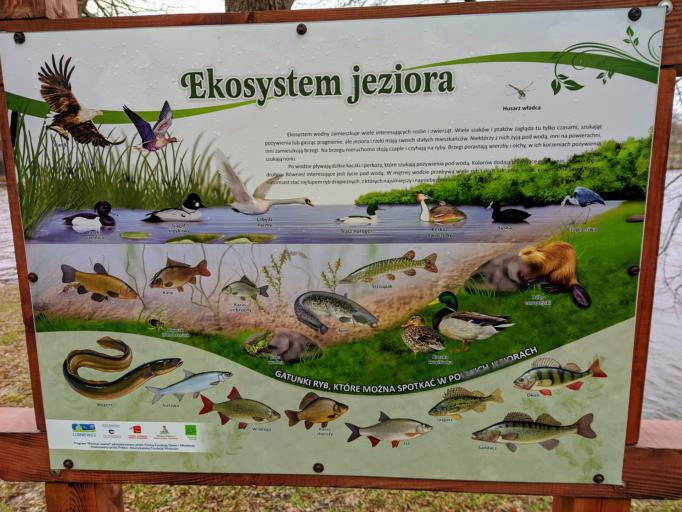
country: PL
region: Lubusz
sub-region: Powiat sulecinski
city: Lubniewice
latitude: 52.5165
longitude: 15.2455
